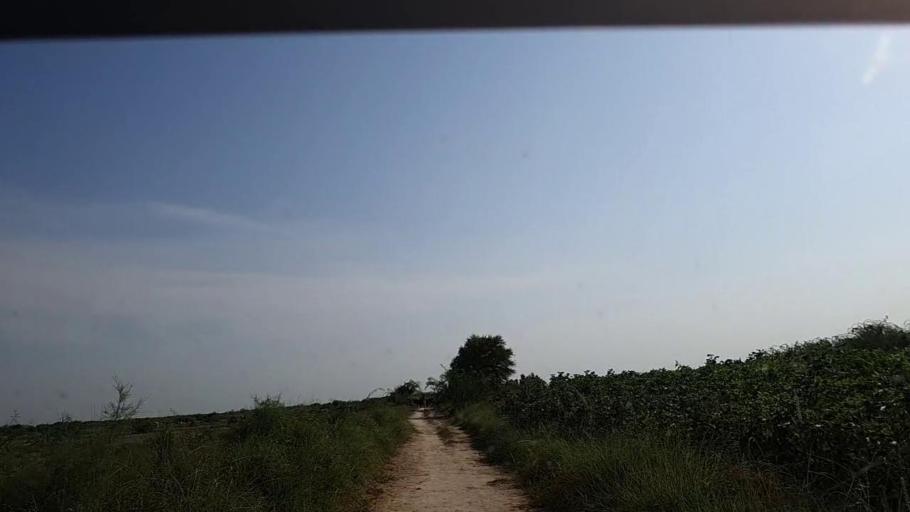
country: PK
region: Sindh
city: Adilpur
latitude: 27.9063
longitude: 69.2350
